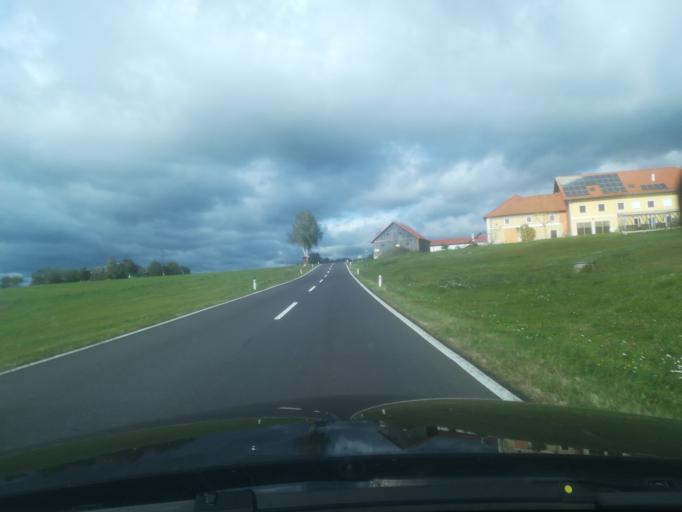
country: AT
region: Upper Austria
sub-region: Politischer Bezirk Urfahr-Umgebung
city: Gramastetten
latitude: 48.3964
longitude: 14.1812
